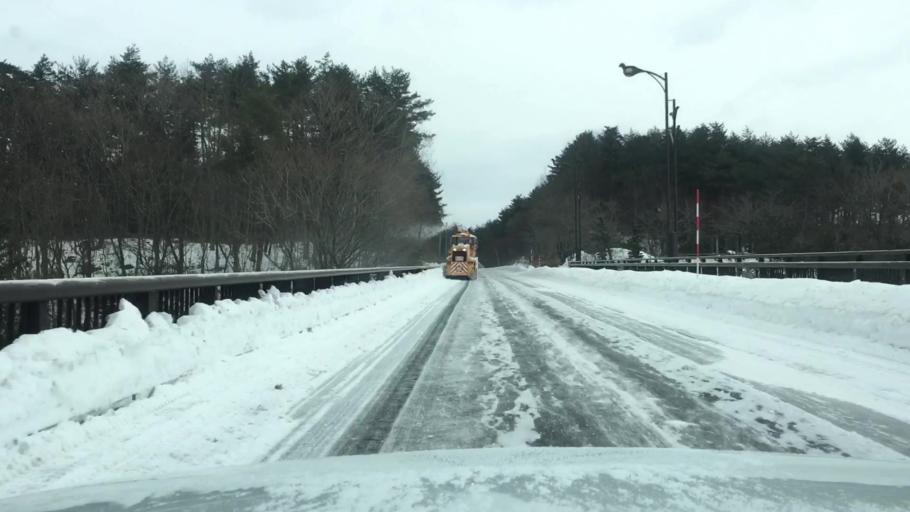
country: JP
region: Iwate
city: Shizukuishi
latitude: 39.9454
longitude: 140.9974
